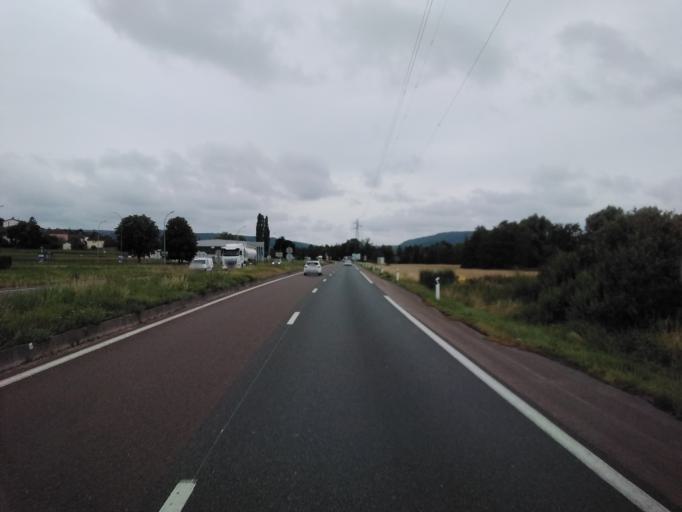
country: FR
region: Franche-Comte
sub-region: Departement de la Haute-Saone
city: Noidans-les-Vesoul
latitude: 47.6305
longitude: 6.1382
